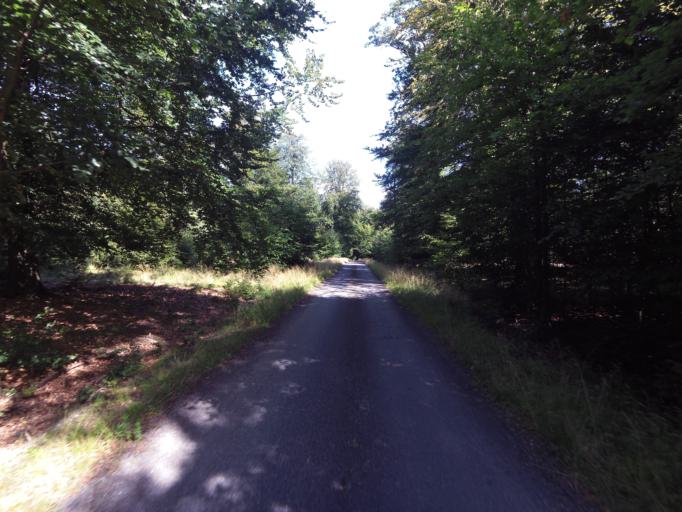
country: BE
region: Wallonia
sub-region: Province du Luxembourg
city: Nassogne
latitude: 50.1088
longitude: 5.3830
